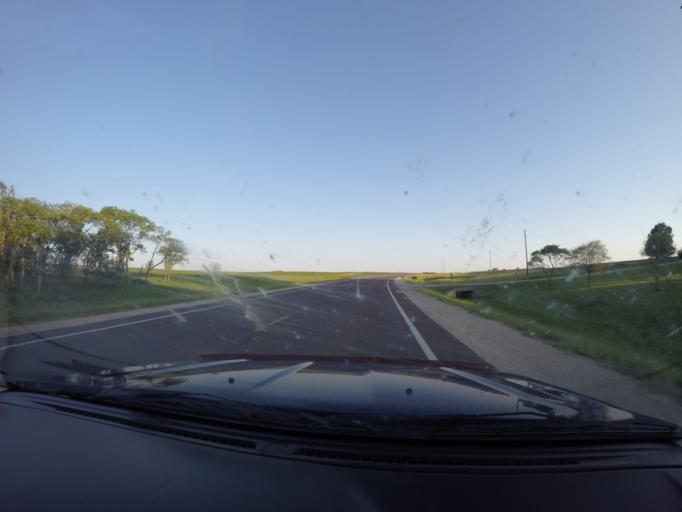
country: US
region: Kansas
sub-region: Marshall County
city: Blue Rapids
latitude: 39.5721
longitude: -96.7506
